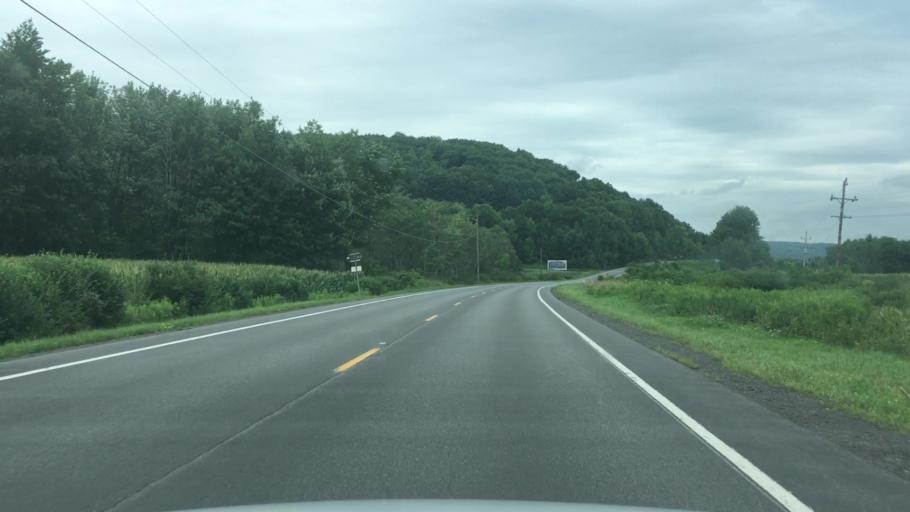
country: US
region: New York
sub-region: Otsego County
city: West End
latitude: 42.4317
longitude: -75.1280
